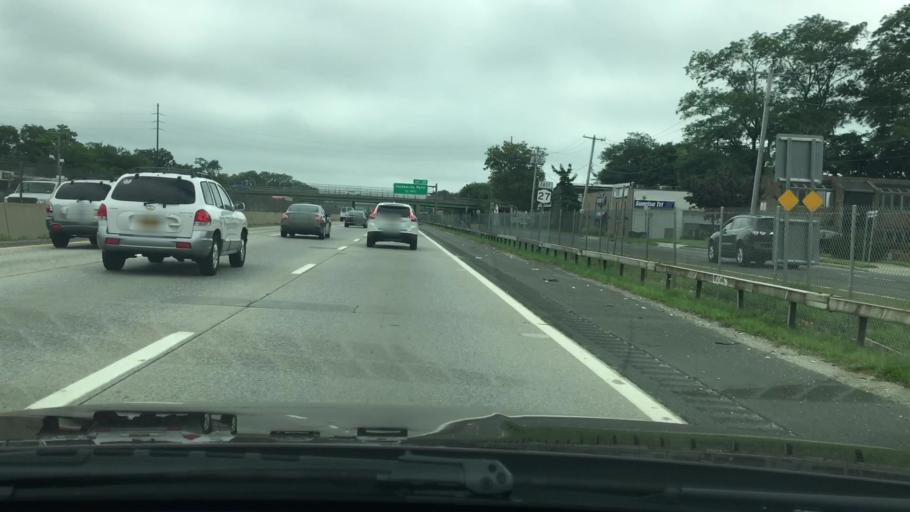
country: US
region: New York
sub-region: Suffolk County
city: West Babylon
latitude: 40.7131
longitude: -73.3539
